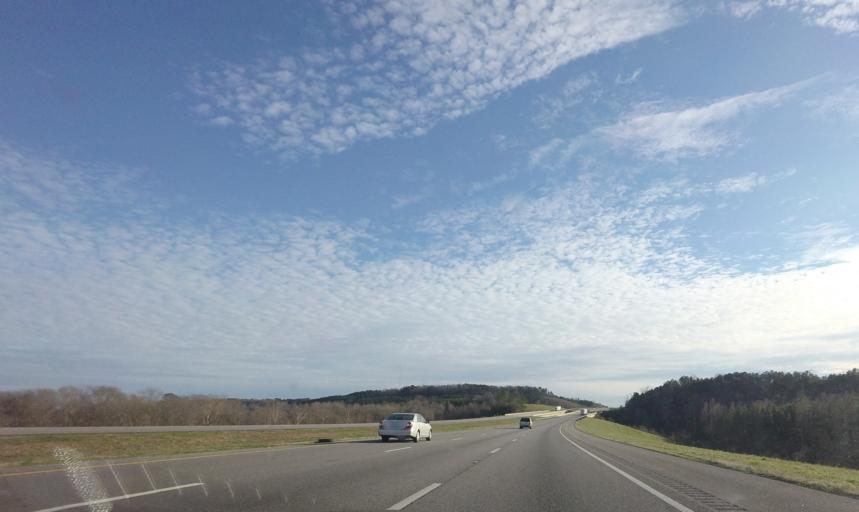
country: US
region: Alabama
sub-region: Walker County
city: Cordova
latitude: 33.7796
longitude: -87.2101
